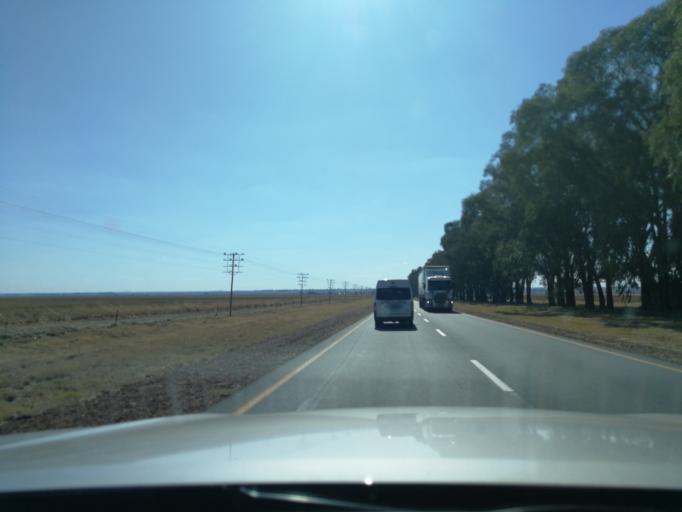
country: ZA
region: North-West
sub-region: Ngaka Modiri Molema District Municipality
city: Lichtenburg
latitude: -26.2324
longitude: 26.2184
